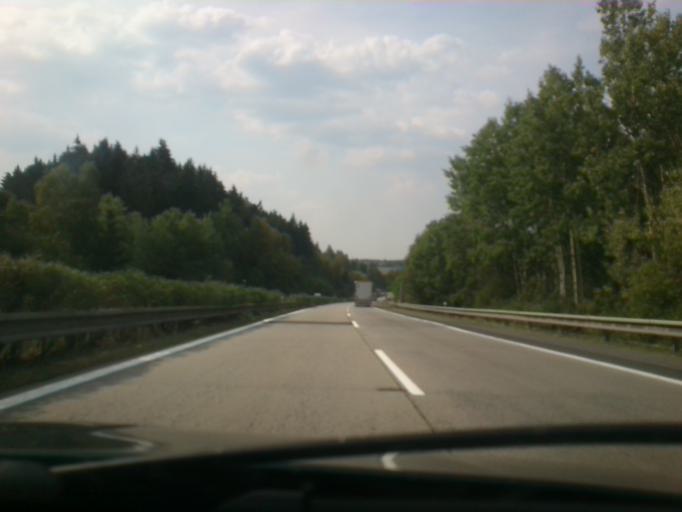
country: CZ
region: Central Bohemia
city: Divisov
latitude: 49.8116
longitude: 14.8836
